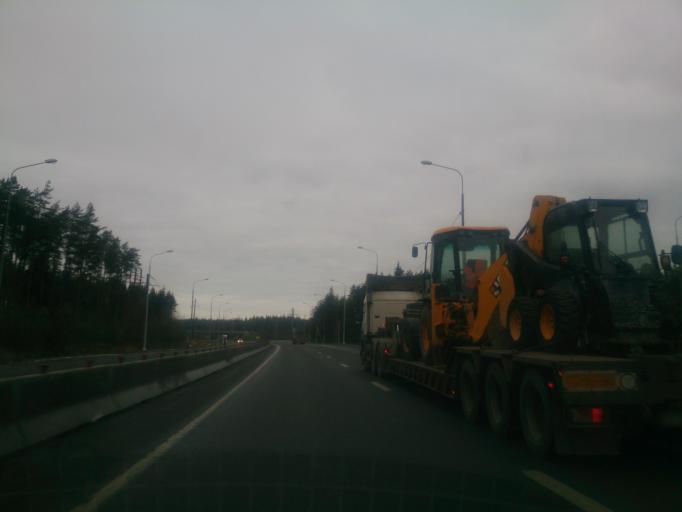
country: RU
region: Leningrad
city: Nurma
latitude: 59.4908
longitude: 30.9682
